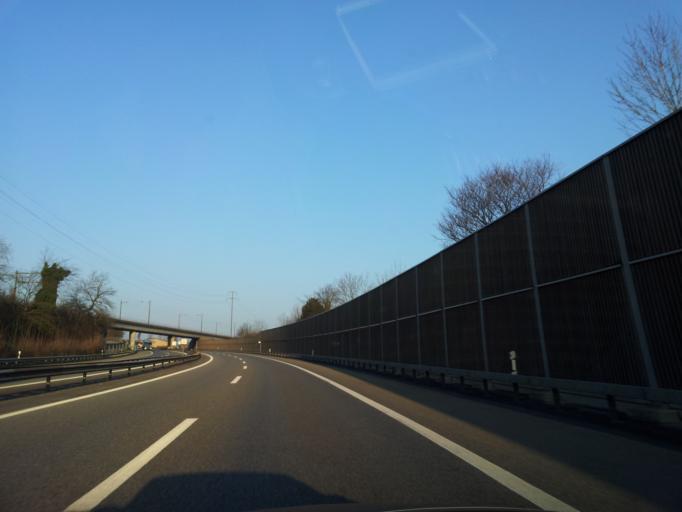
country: CH
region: Aargau
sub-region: Bezirk Rheinfelden
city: Mumpf
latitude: 47.5504
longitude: 7.9048
